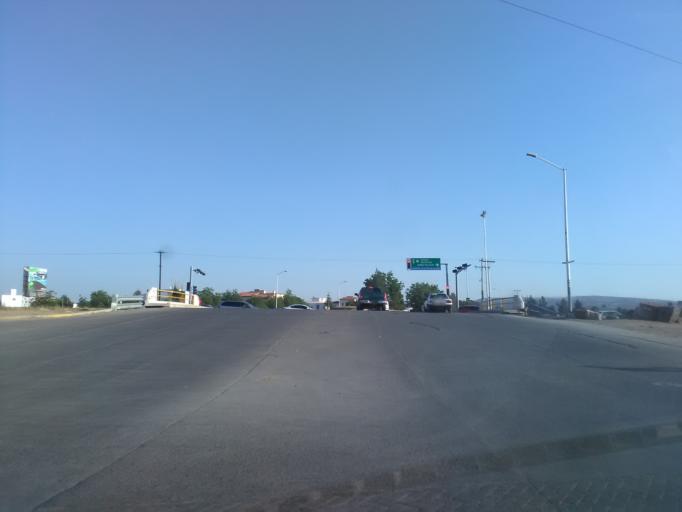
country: MX
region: Durango
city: Victoria de Durango
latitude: 24.0610
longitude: -104.6318
